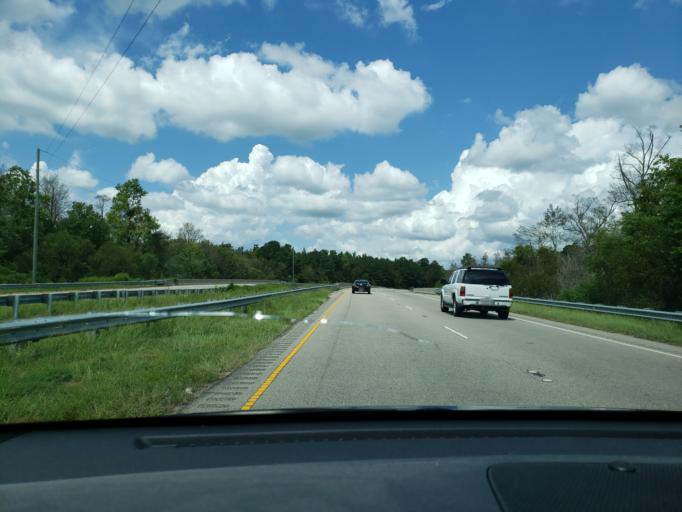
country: US
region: North Carolina
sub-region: Bladen County
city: Elizabethtown
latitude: 34.6776
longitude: -78.7409
